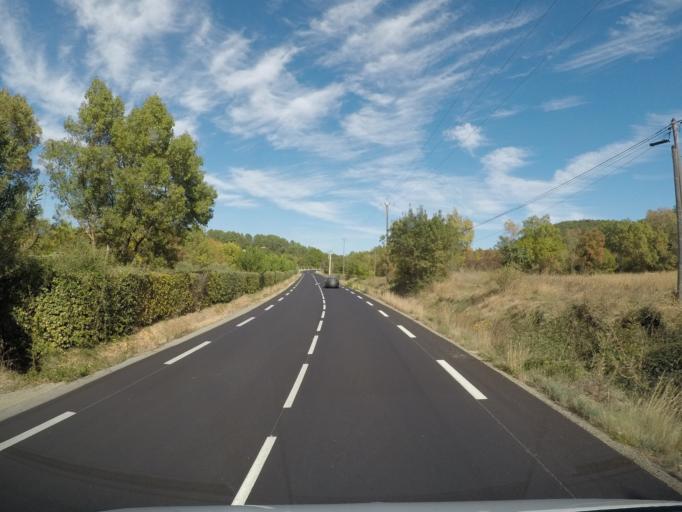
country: FR
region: Languedoc-Roussillon
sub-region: Departement du Gard
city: Sauve
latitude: 43.9841
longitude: 3.9347
